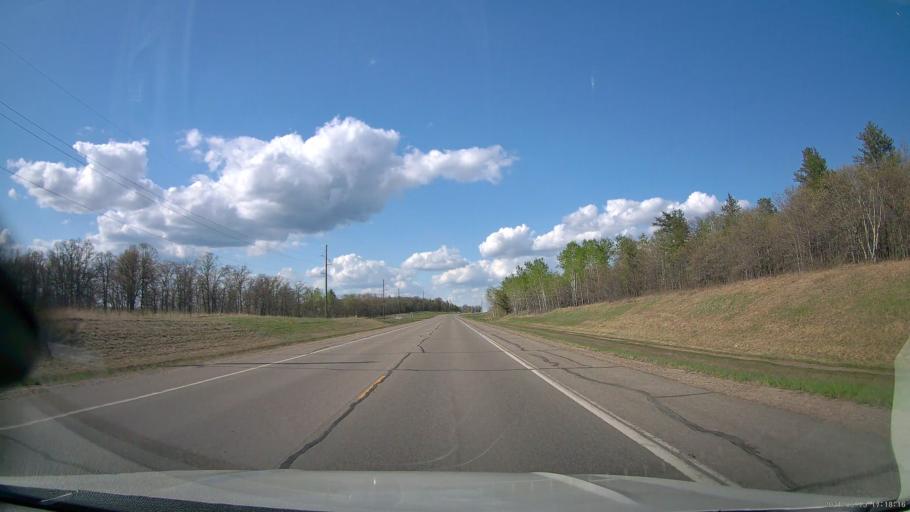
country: US
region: Minnesota
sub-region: Hubbard County
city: Park Rapids
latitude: 46.9585
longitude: -95.0184
